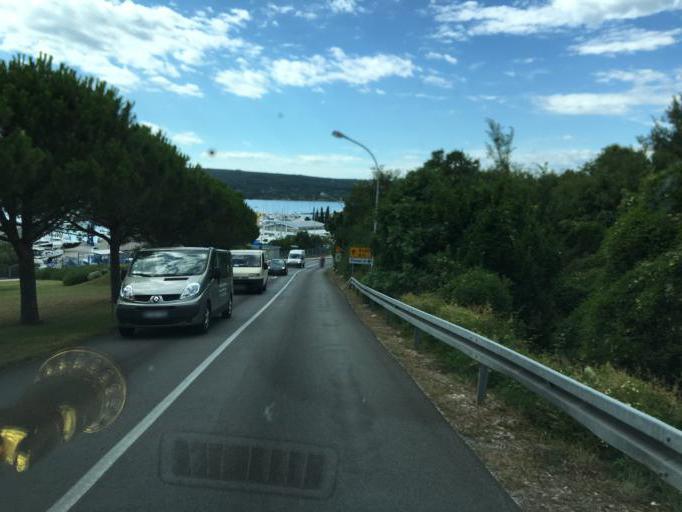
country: HR
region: Primorsko-Goranska
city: Punat
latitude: 45.0255
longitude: 14.6320
